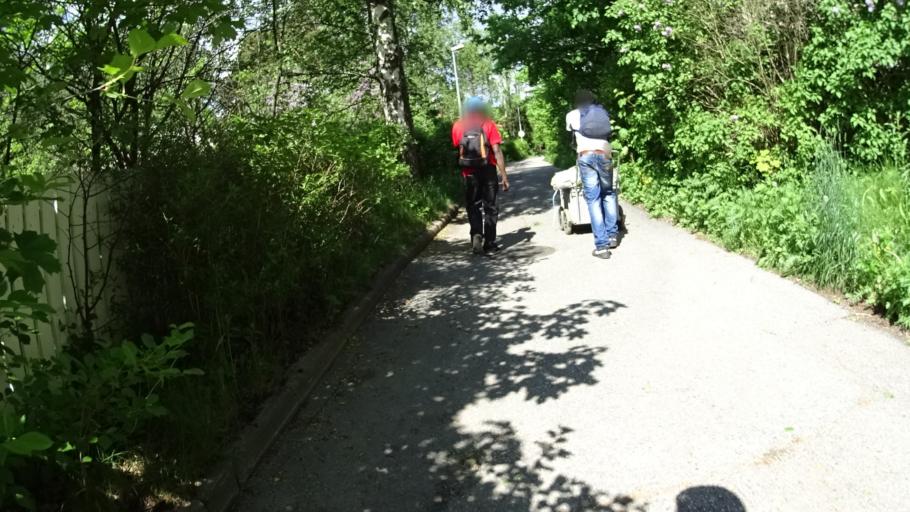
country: FI
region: Uusimaa
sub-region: Helsinki
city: Kauniainen
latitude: 60.1972
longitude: 24.7508
